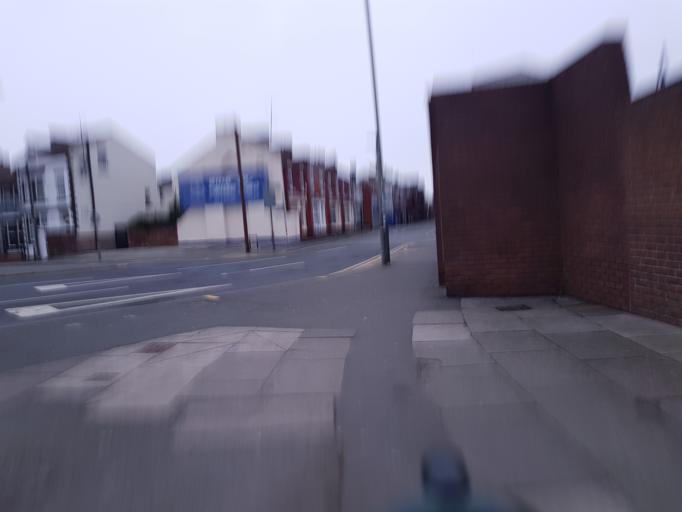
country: GB
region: England
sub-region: Liverpool
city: Liverpool
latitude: 53.4375
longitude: -2.9676
